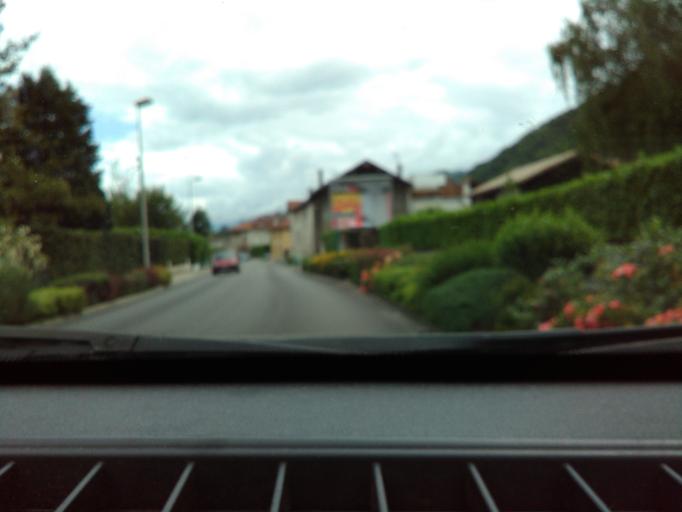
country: FR
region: Rhone-Alpes
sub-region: Departement de l'Isere
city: Gieres
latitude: 45.1825
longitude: 5.7962
